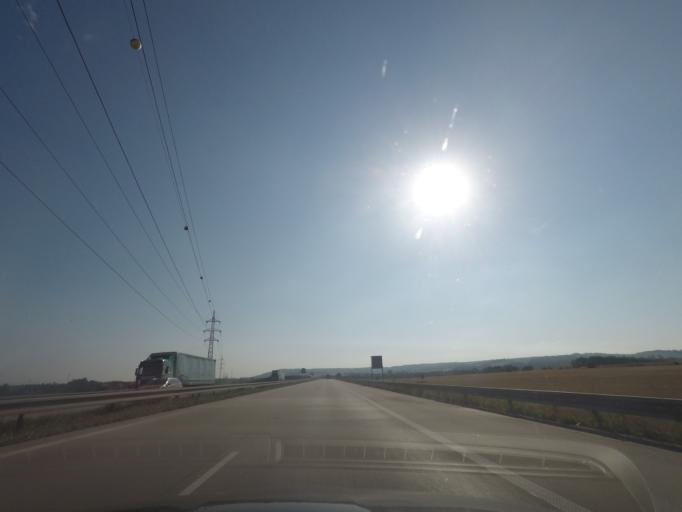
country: CZ
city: Fulnek
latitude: 49.6922
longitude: 17.9616
